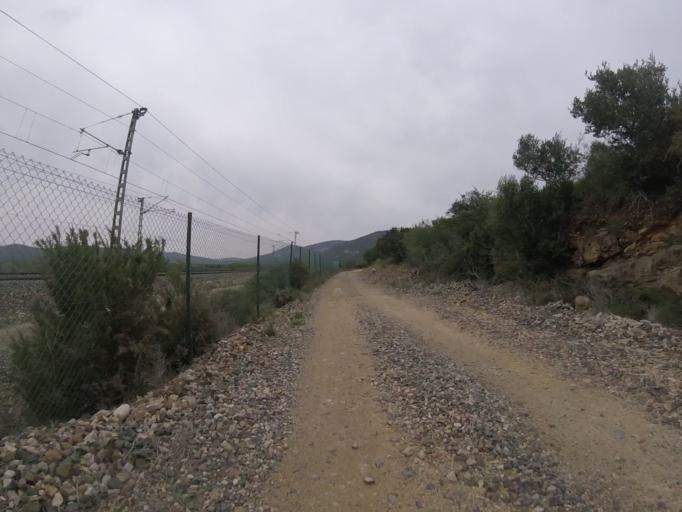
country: ES
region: Valencia
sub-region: Provincia de Castello
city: Alcoceber
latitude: 40.2529
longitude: 0.2502
